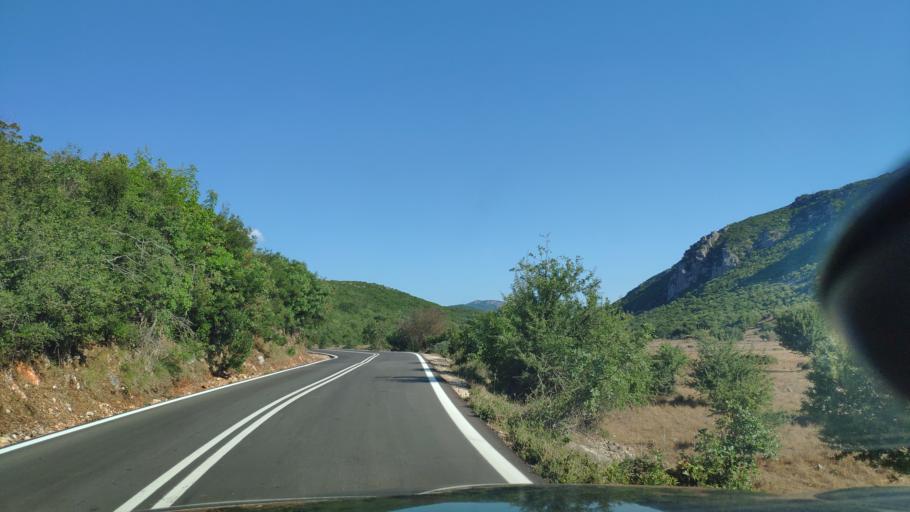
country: GR
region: West Greece
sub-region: Nomos Aitolias kai Akarnanias
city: Fitiai
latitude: 38.6712
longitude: 21.1402
